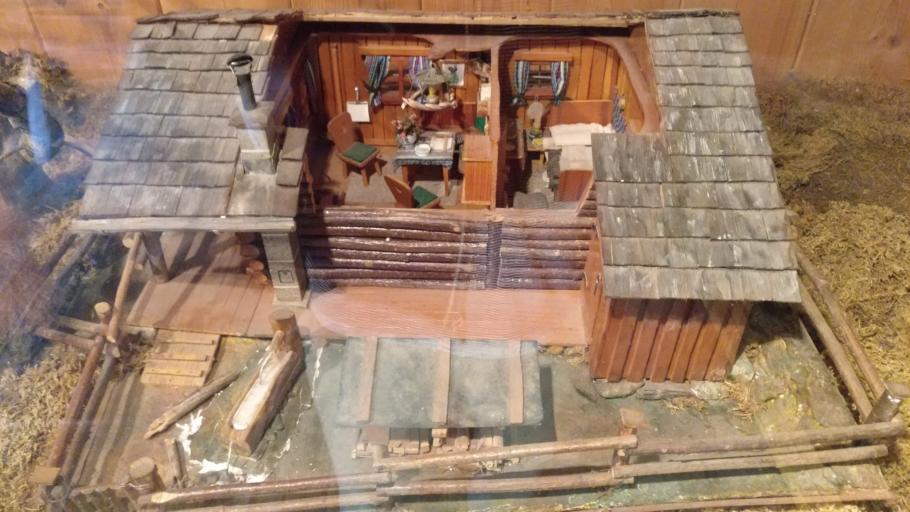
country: AT
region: Salzburg
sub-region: Politischer Bezirk Zell am See
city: Bramberg am Wildkogel
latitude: 47.2702
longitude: 12.3378
